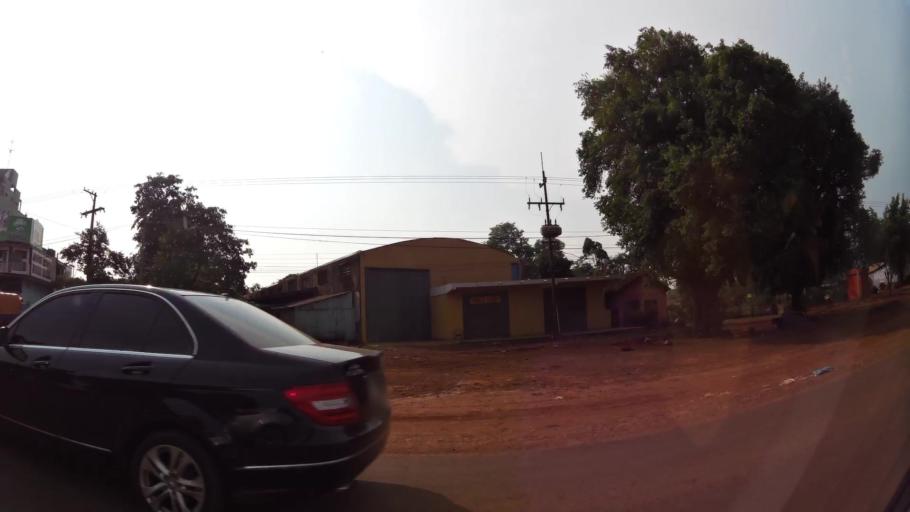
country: PY
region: Alto Parana
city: Ciudad del Este
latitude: -25.4753
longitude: -54.6511
